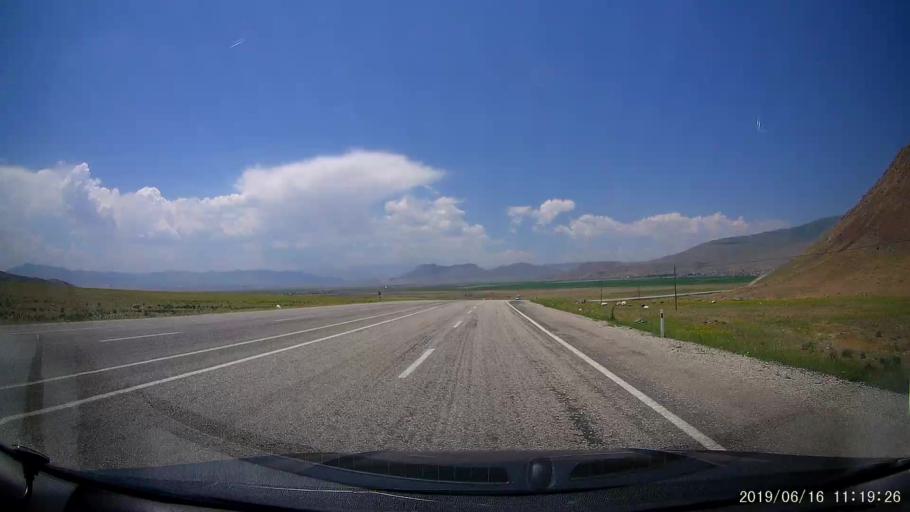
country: TR
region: Agri
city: Dogubayazit
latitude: 39.6985
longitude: 44.1144
